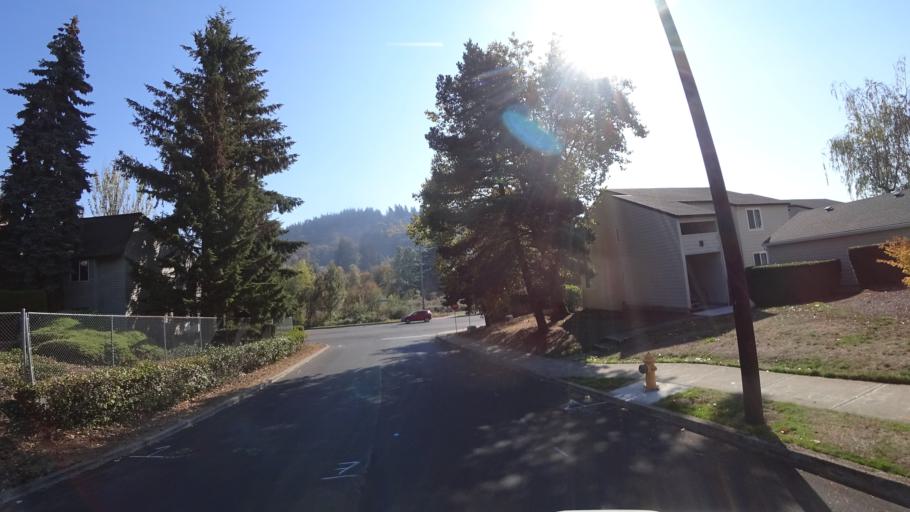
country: US
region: Oregon
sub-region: Multnomah County
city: Gresham
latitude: 45.4952
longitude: -122.4423
